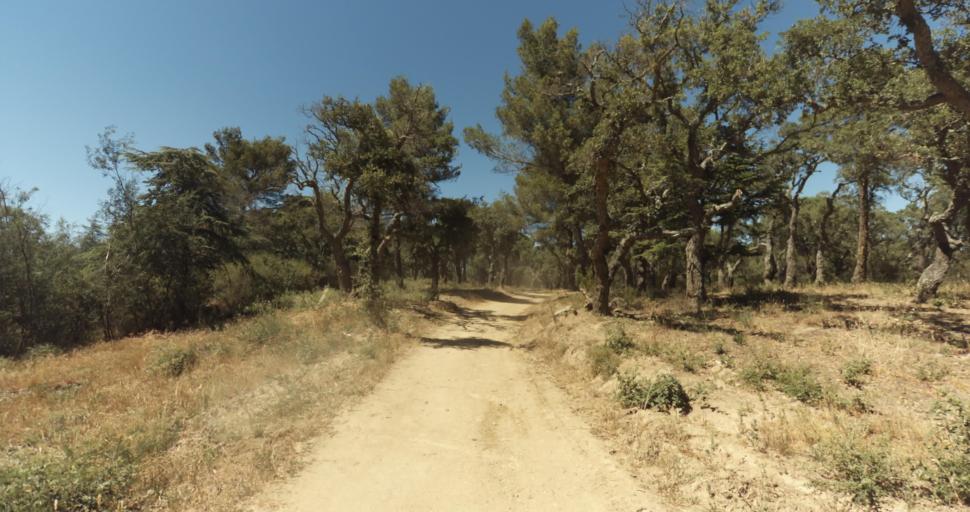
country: FR
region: Provence-Alpes-Cote d'Azur
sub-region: Departement du Var
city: Gassin
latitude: 43.2475
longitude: 6.5620
